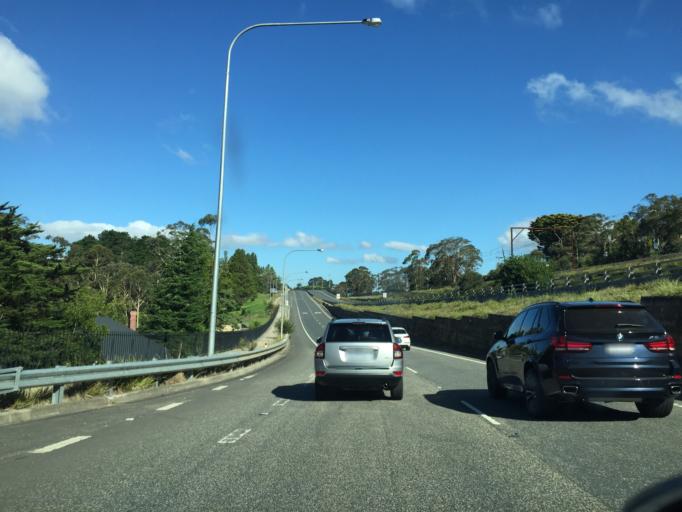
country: AU
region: New South Wales
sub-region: Blue Mountains Municipality
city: Leura
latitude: -33.7080
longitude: 150.3235
